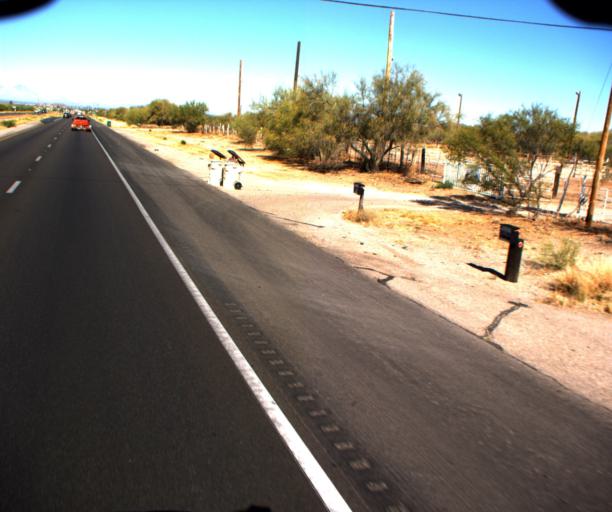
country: US
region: Arizona
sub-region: Pima County
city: Tucson Estates
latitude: 32.1756
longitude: -111.0563
